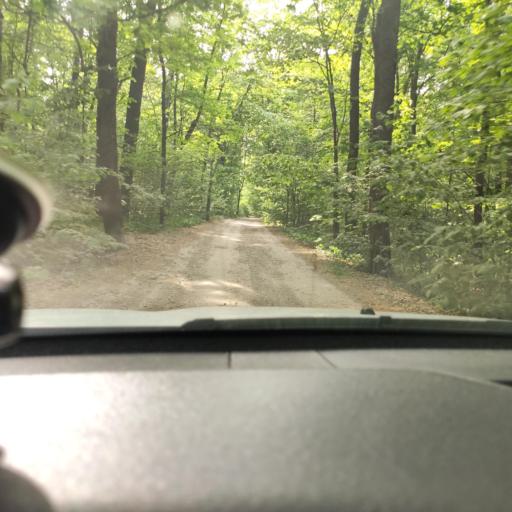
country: RU
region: Samara
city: Volzhskiy
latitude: 53.3272
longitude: 50.2153
